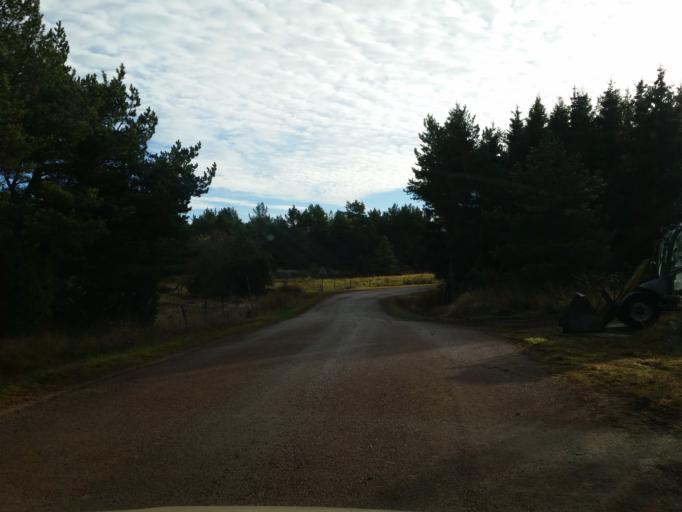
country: AX
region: Alands skaergard
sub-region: Kumlinge
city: Kumlinge
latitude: 60.2647
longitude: 20.7729
